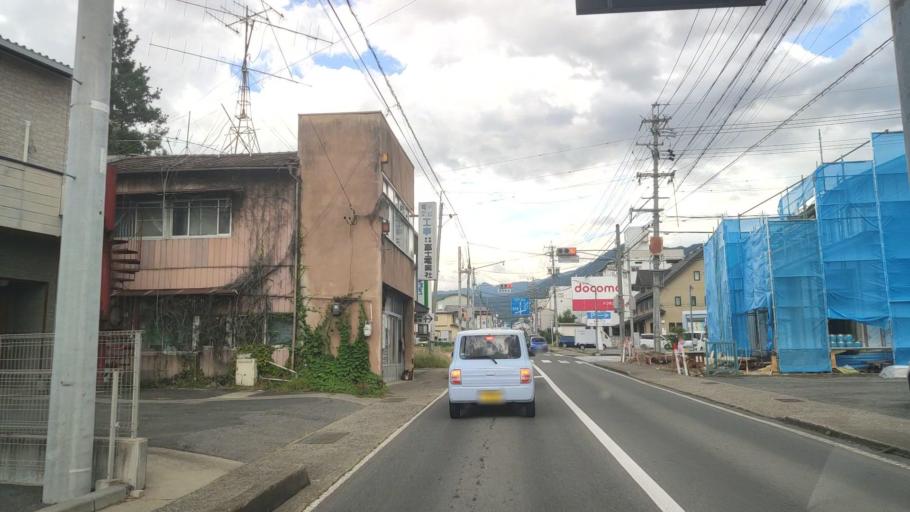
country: JP
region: Nagano
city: Suzaka
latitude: 36.6546
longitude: 138.3036
